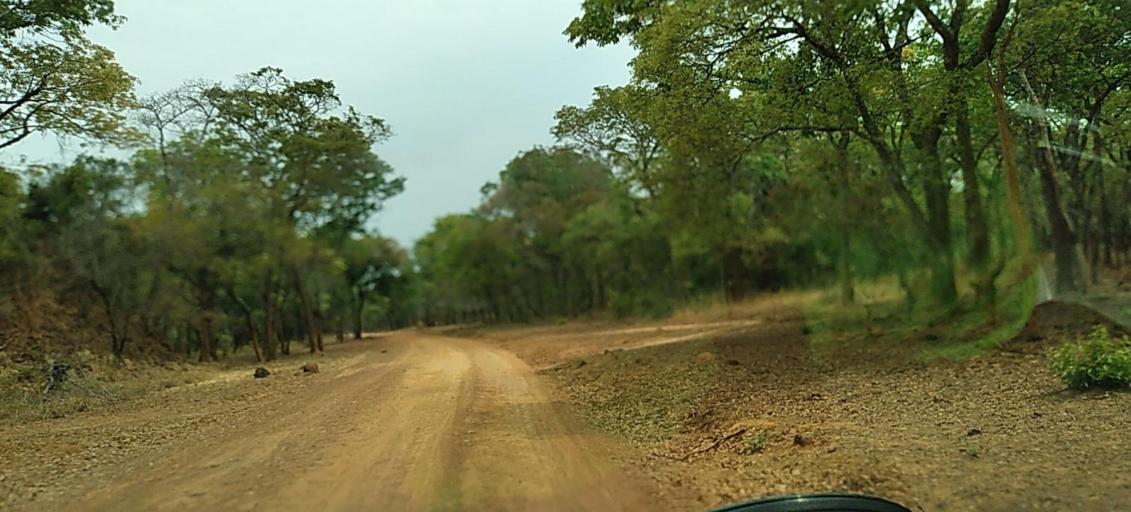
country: ZM
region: North-Western
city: Solwezi
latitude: -12.9416
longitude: 26.5579
